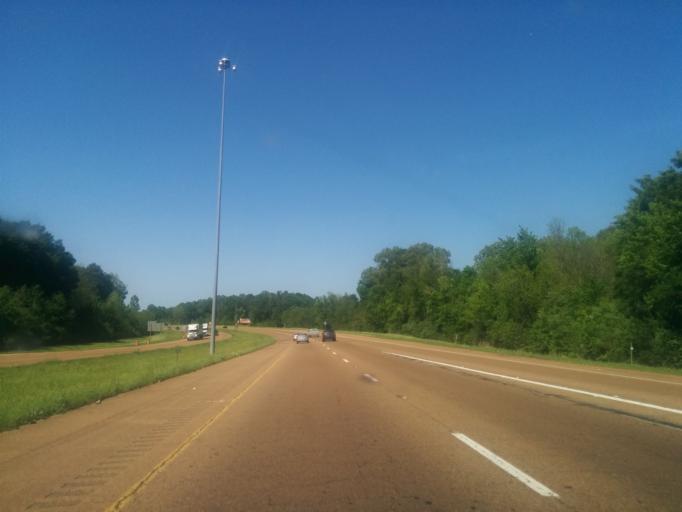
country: US
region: Mississippi
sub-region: Madison County
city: Madison
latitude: 32.4742
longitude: -90.1320
